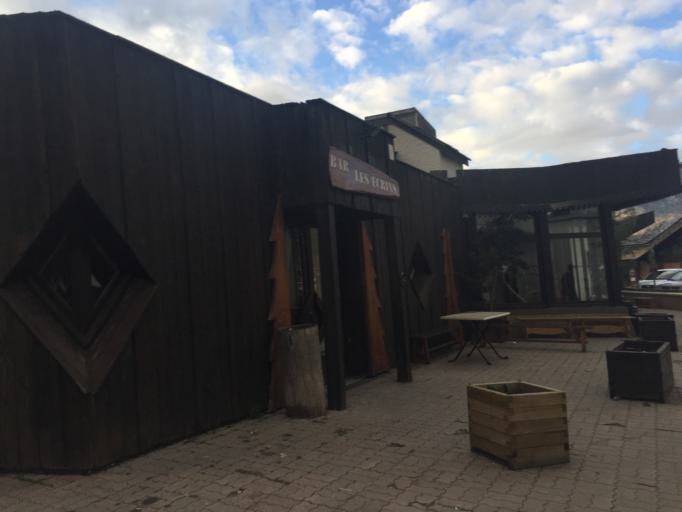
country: FR
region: Provence-Alpes-Cote d'Azur
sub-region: Departement des Hautes-Alpes
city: Embrun
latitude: 44.4933
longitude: 6.5563
